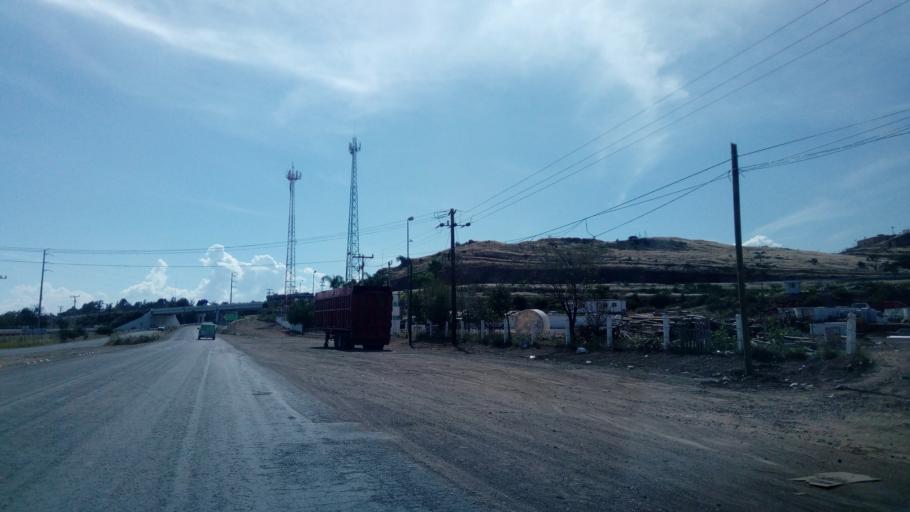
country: MX
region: Durango
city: Victoria de Durango
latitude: 24.0714
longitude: -104.6569
